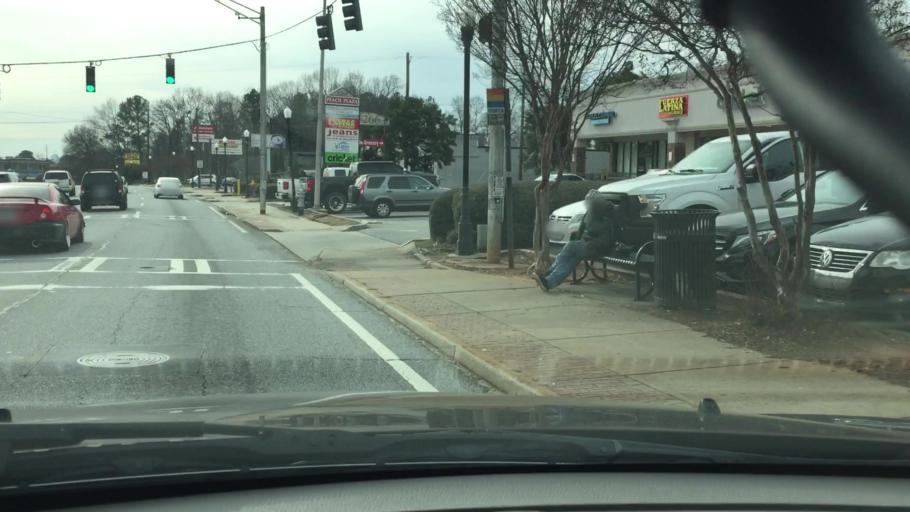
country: US
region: Georgia
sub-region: DeKalb County
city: Doraville
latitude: 33.8966
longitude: -84.2819
